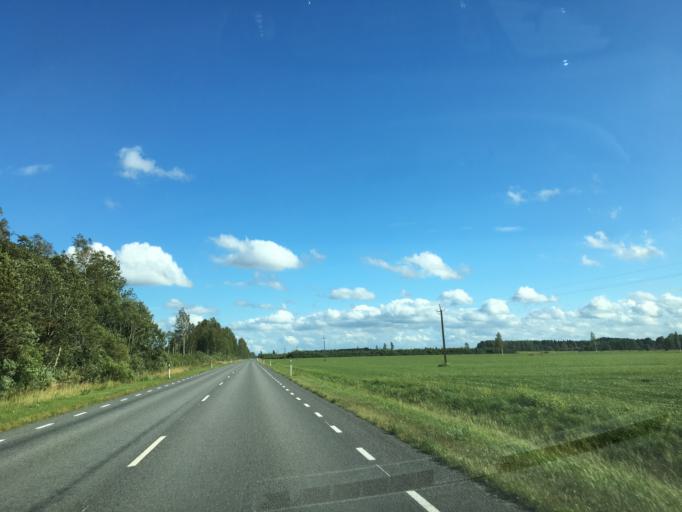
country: EE
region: Paernumaa
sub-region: Vaendra vald (alev)
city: Vandra
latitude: 58.6030
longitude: 25.1327
